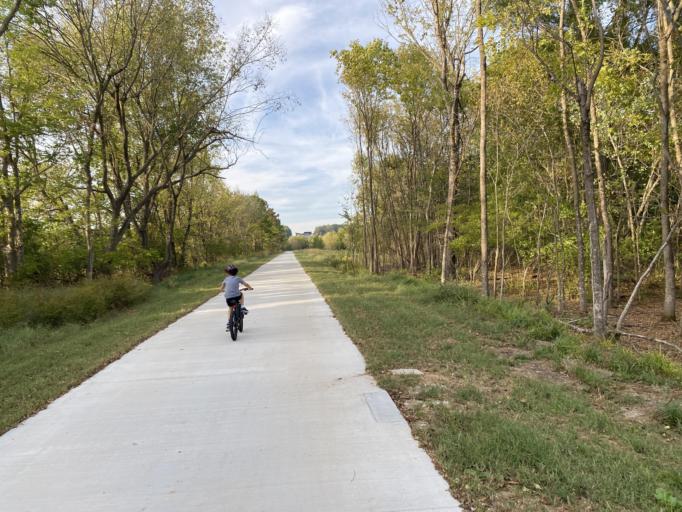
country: US
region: Arkansas
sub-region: Washington County
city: Johnson
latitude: 36.1068
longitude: -94.1942
